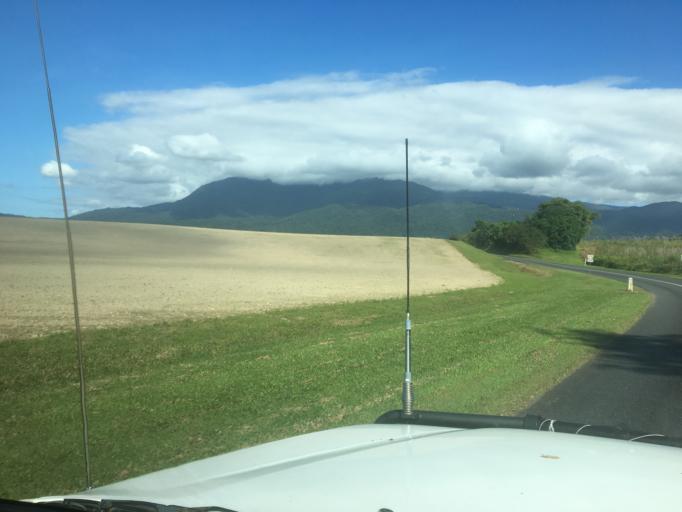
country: AU
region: Queensland
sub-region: Cassowary Coast
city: Innisfail
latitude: -17.3474
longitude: 145.9054
